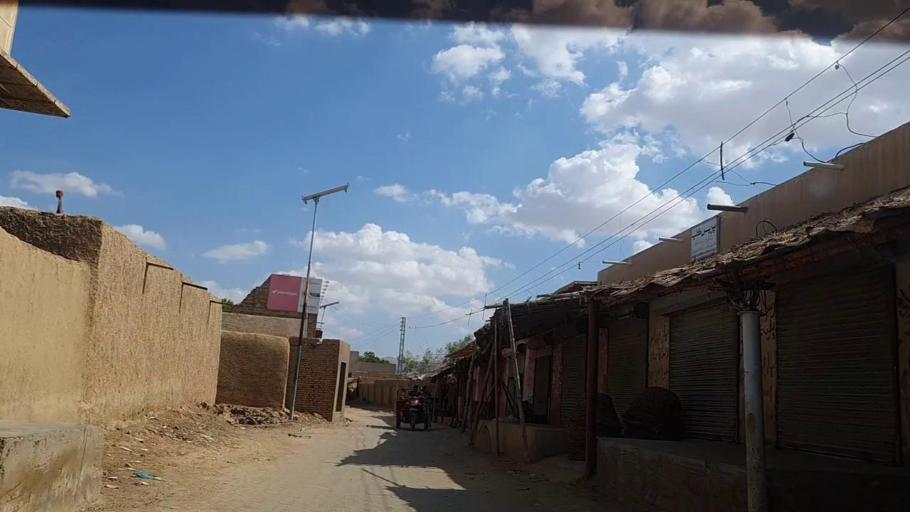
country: PK
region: Sindh
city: Johi
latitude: 26.4967
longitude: 67.4316
